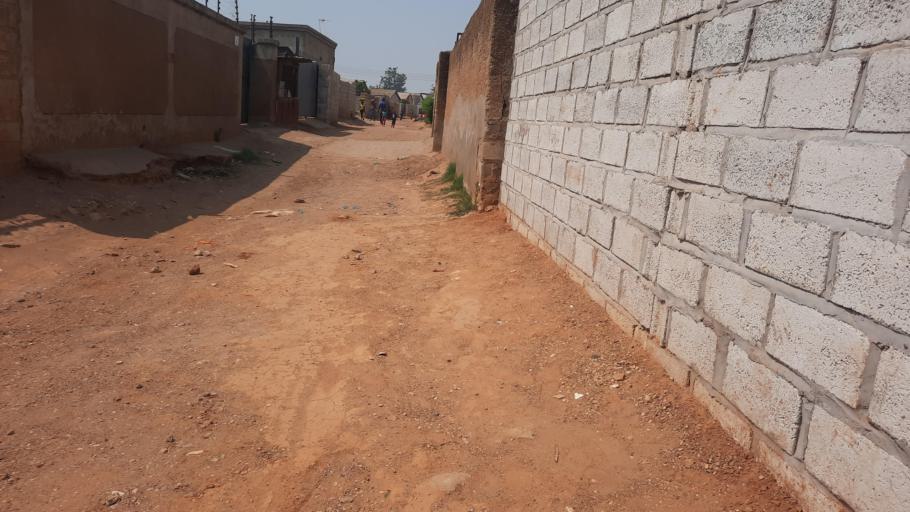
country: ZM
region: Lusaka
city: Lusaka
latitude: -15.3943
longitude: 28.3823
